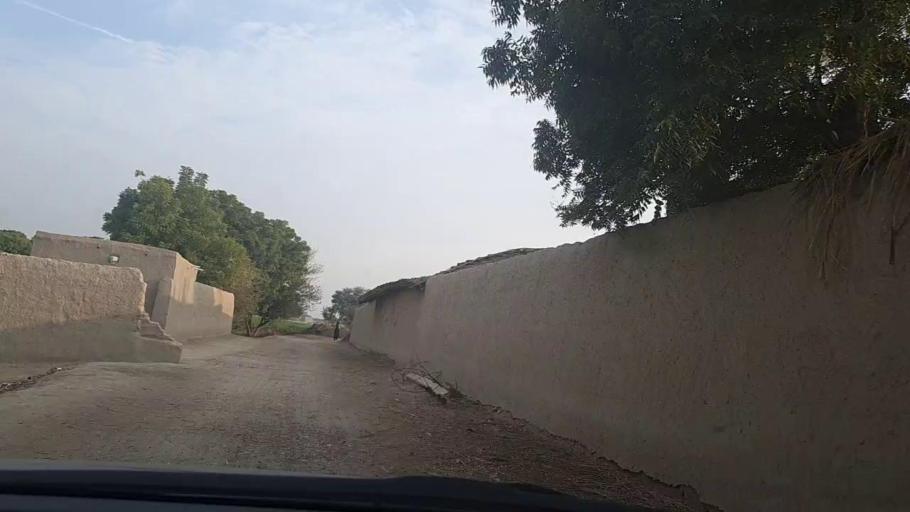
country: PK
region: Sindh
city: Daulatpur
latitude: 26.3314
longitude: 68.0239
